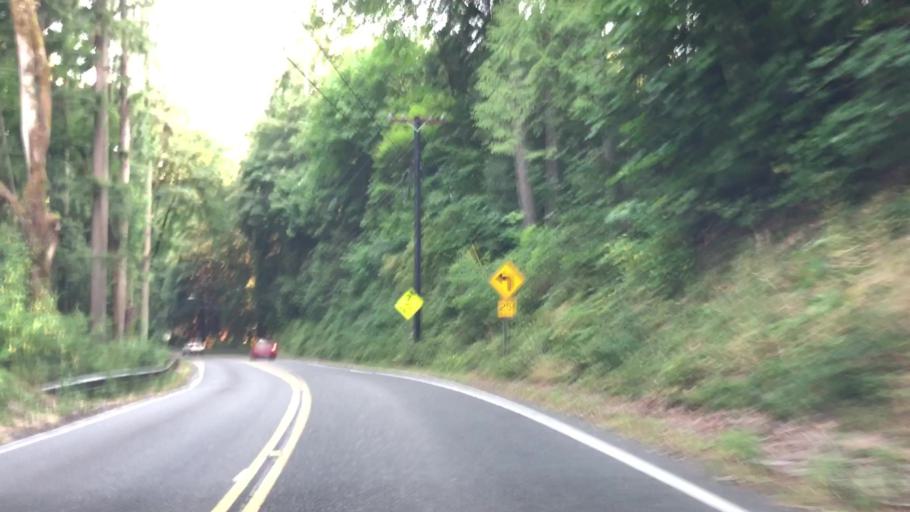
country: US
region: Washington
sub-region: King County
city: Sammamish
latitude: 47.6741
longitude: -122.0714
